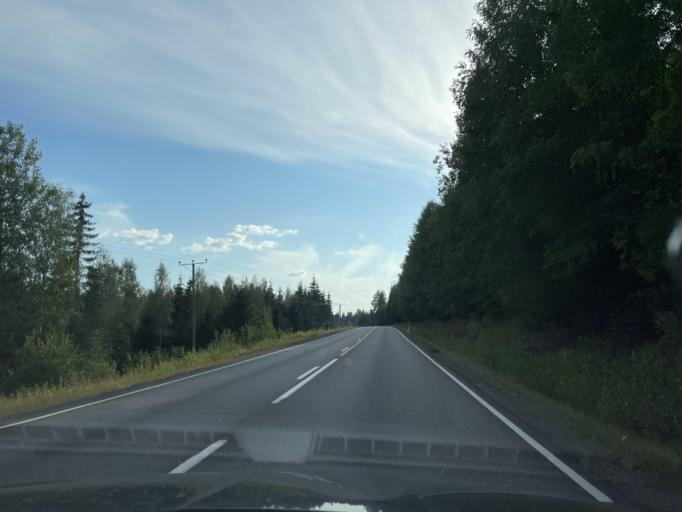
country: FI
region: Paijanne Tavastia
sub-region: Lahti
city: Auttoinen
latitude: 61.3272
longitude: 25.1787
